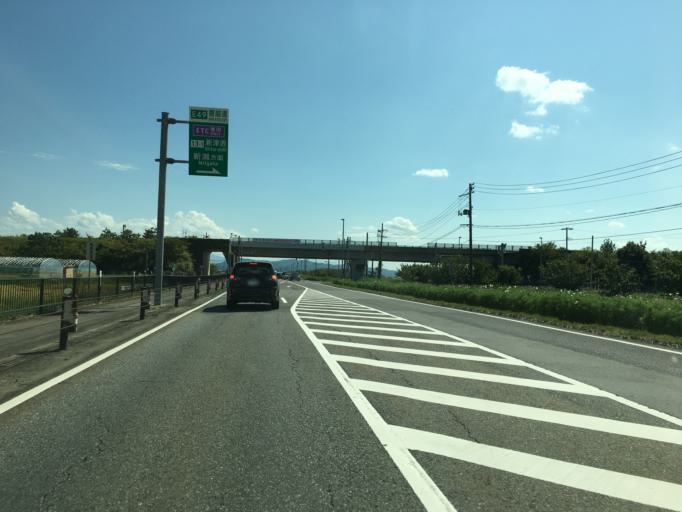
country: JP
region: Niigata
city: Niitsu-honcho
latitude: 37.8221
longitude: 139.0988
